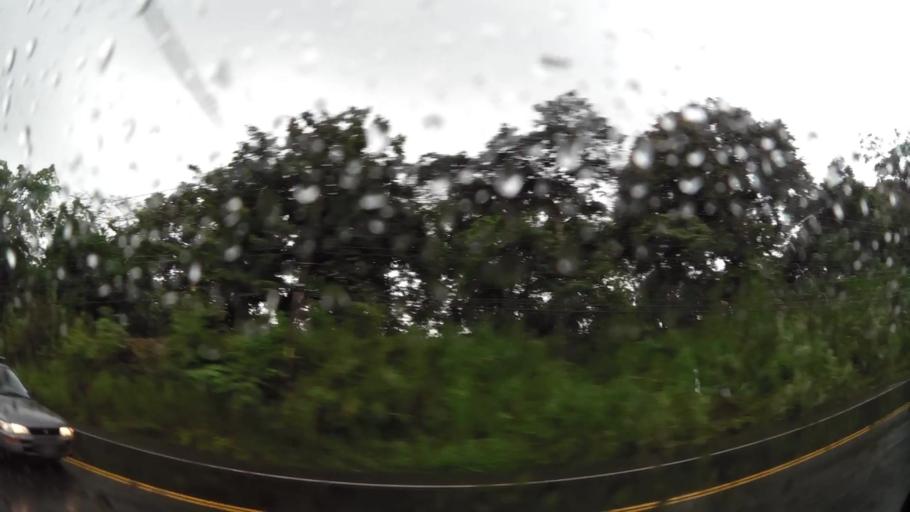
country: PA
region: Colon
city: Buena Vista
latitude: 9.2775
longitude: -79.7018
